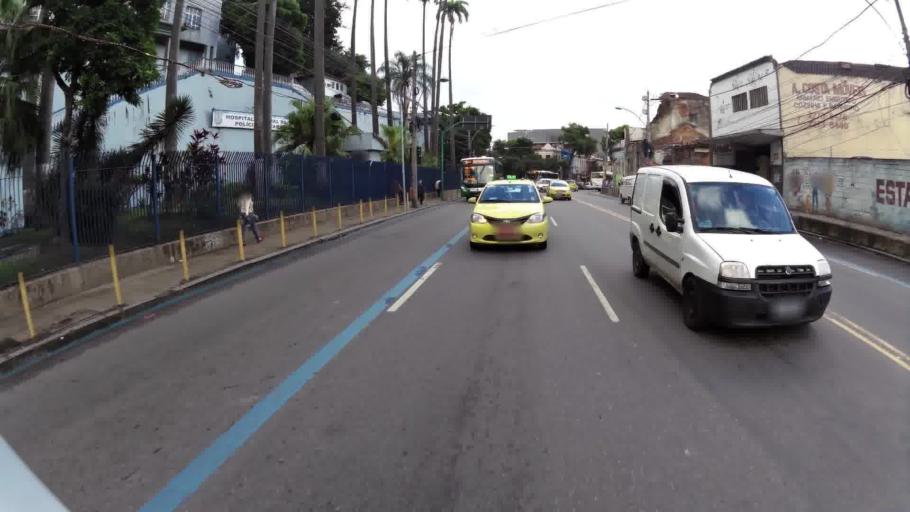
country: BR
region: Rio de Janeiro
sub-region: Rio De Janeiro
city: Rio de Janeiro
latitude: -22.9135
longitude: -43.2038
